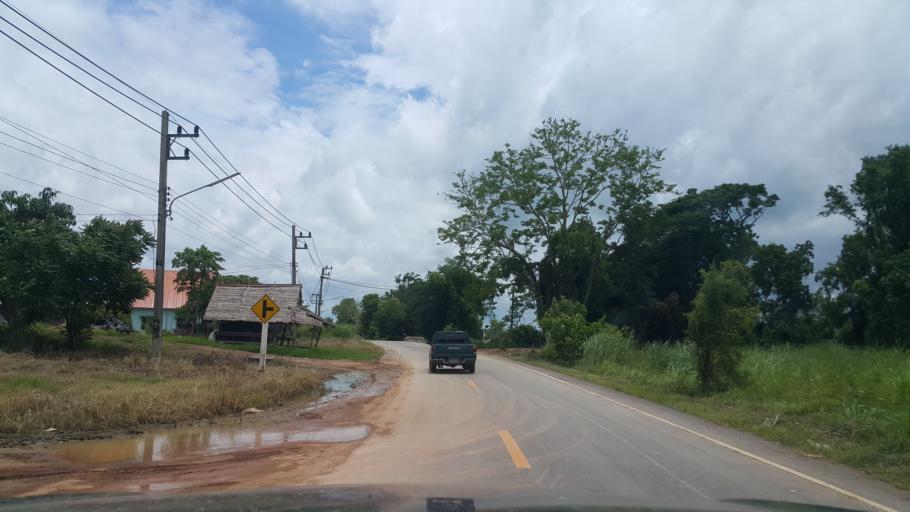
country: TH
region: Sukhothai
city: Kong Krailat
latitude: 16.9341
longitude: 99.9356
